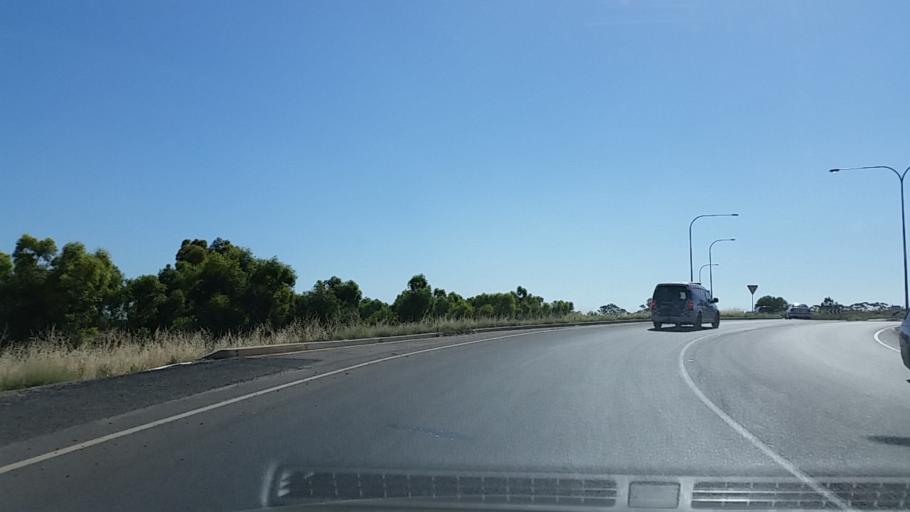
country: AU
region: South Australia
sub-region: Playford
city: Angle Vale
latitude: -34.6637
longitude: 138.6576
